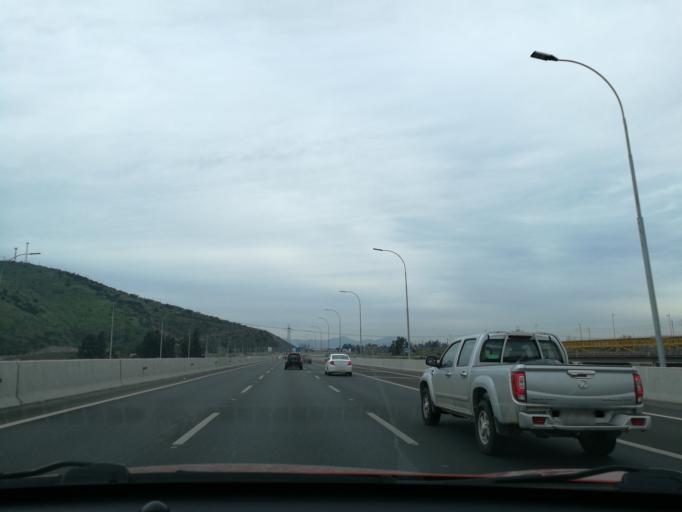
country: CL
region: Santiago Metropolitan
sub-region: Provincia de Maipo
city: Buin
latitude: -33.6920
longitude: -70.7246
